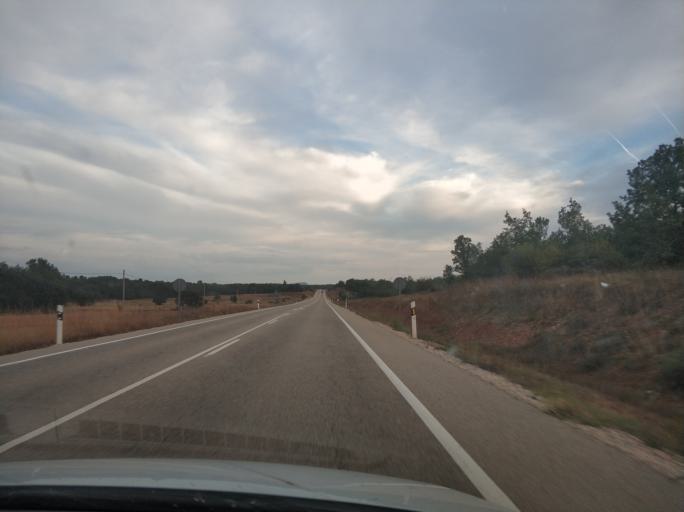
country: ES
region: Castille and Leon
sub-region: Provincia de Burgos
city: Hacinas
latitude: 41.9681
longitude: -3.2952
